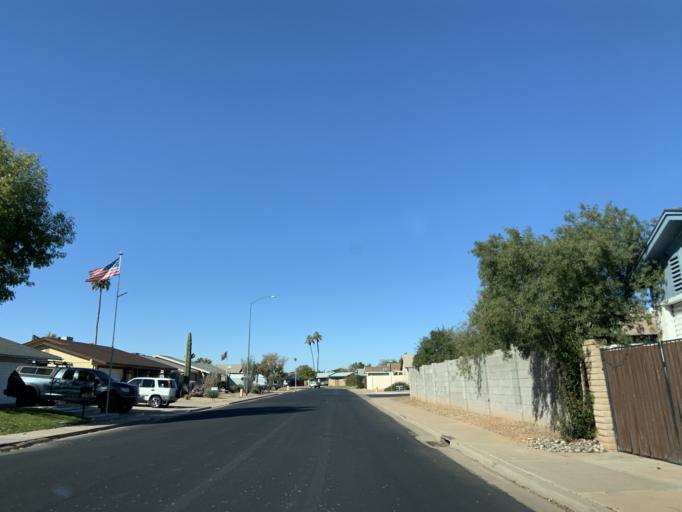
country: US
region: Arizona
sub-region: Maricopa County
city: San Carlos
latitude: 33.3737
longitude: -111.8570
